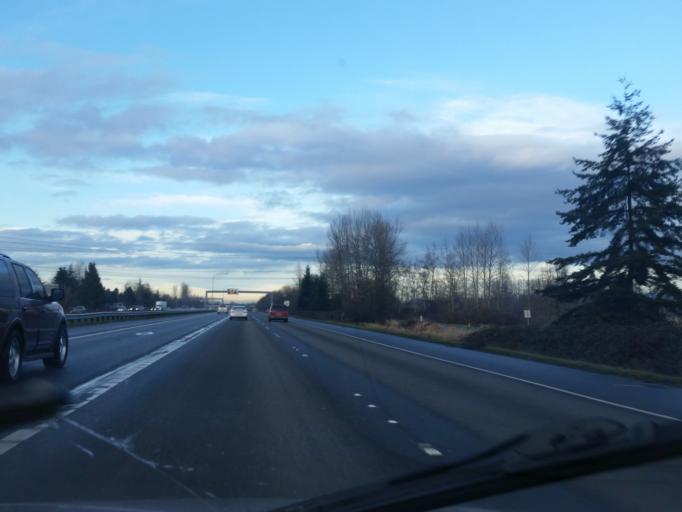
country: US
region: Washington
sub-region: King County
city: Auburn
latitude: 47.3319
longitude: -122.2447
